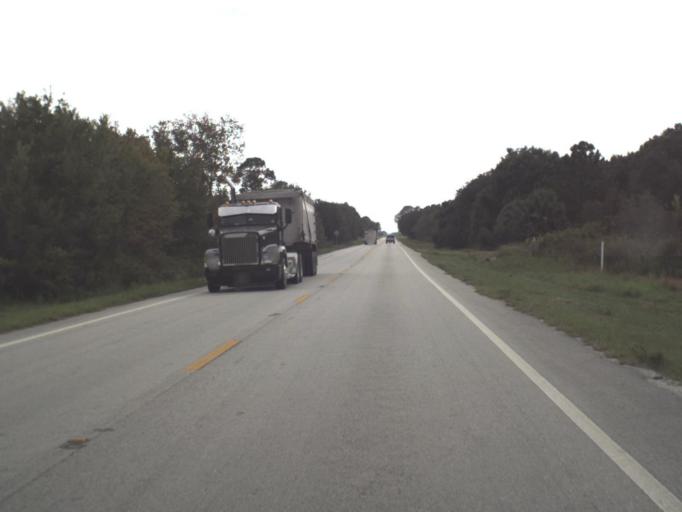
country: US
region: Florida
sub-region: Okeechobee County
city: Cypress Quarters
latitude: 27.3309
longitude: -80.8237
